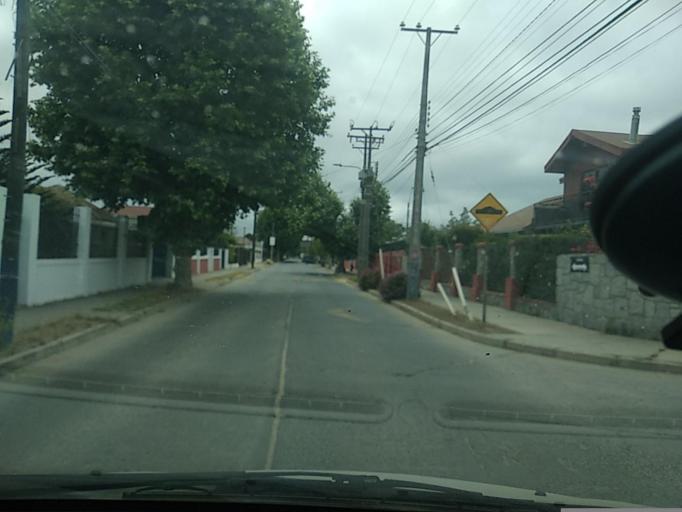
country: CL
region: Valparaiso
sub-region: Provincia de Marga Marga
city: Villa Alemana
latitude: -33.0407
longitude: -71.3692
